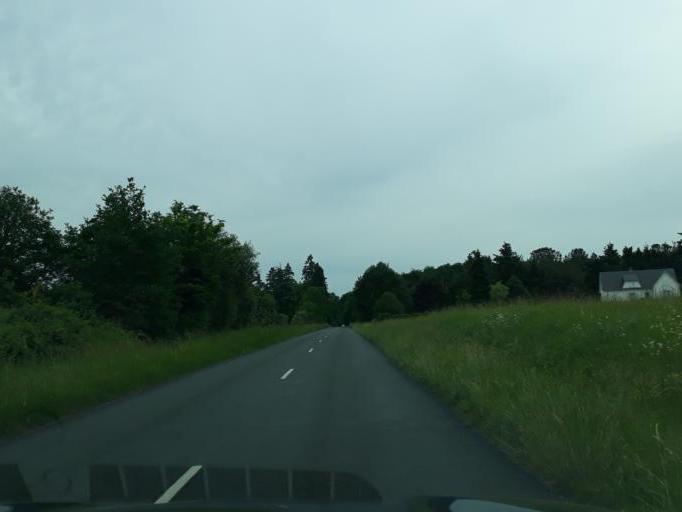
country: FR
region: Centre
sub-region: Departement du Loiret
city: Saint-Pere-sur-Loire
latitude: 47.7490
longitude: 2.3575
